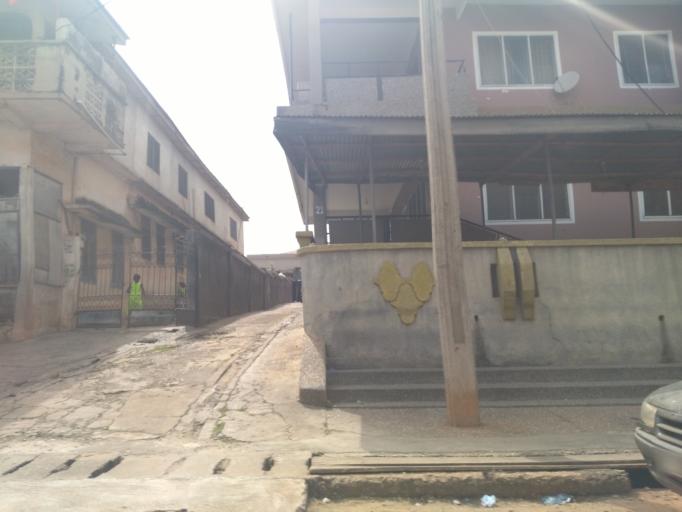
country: GH
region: Ashanti
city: Kumasi
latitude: 6.6843
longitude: -1.5976
